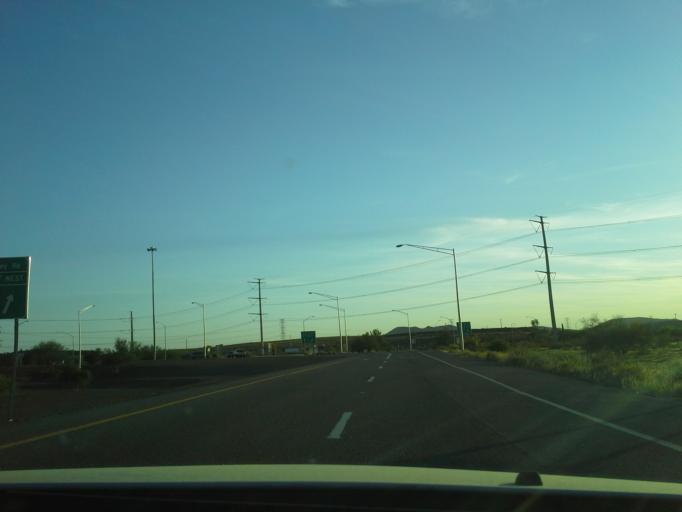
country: US
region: Arizona
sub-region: Maricopa County
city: Anthem
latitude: 33.7145
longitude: -112.1193
